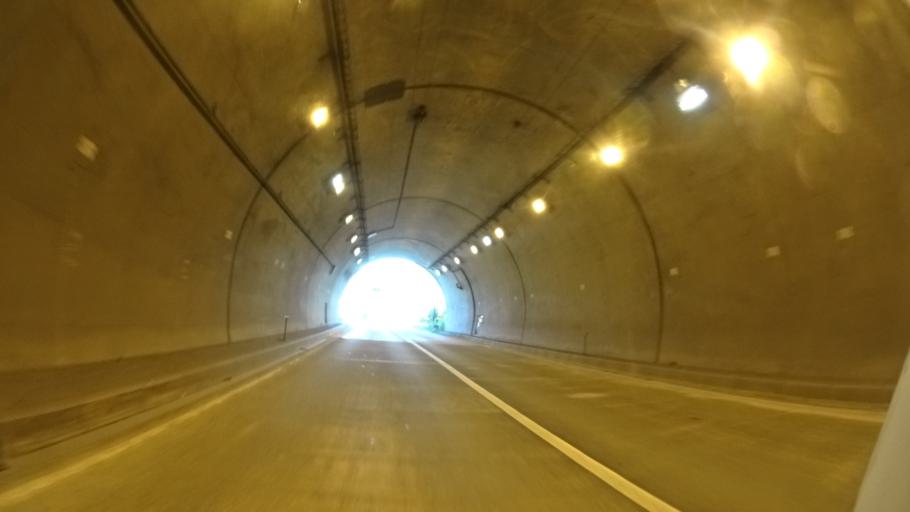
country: JP
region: Fukui
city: Tsuruga
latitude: 35.6214
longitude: 136.0826
